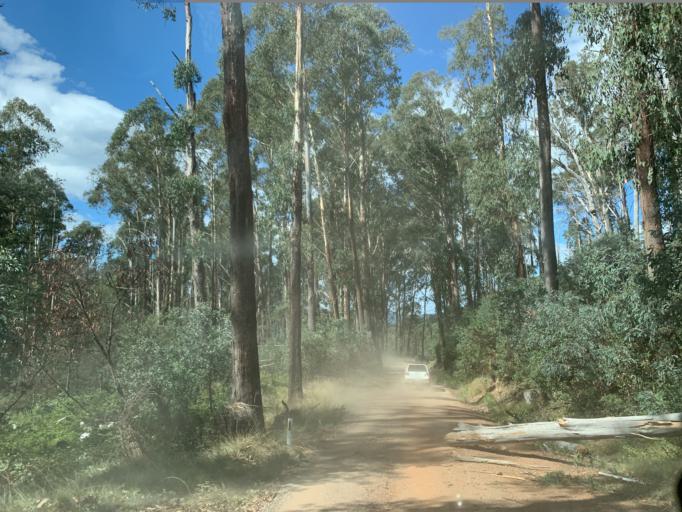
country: AU
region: Victoria
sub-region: Mansfield
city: Mansfield
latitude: -37.0969
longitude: 146.5337
